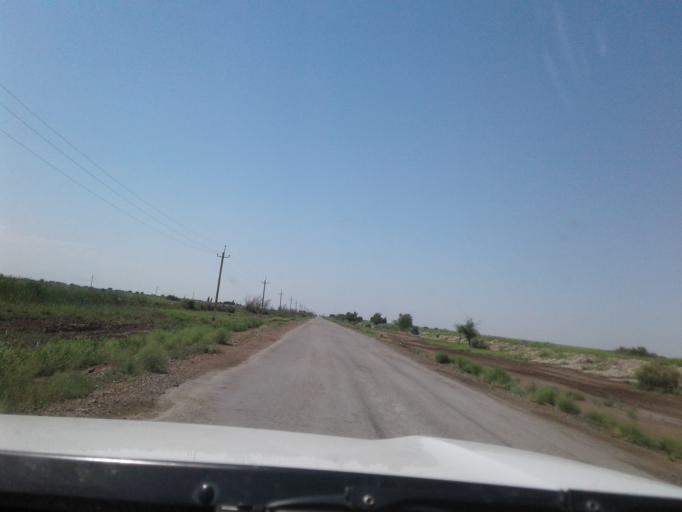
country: TM
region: Dasoguz
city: Koeneuergench
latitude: 41.8610
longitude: 58.7055
